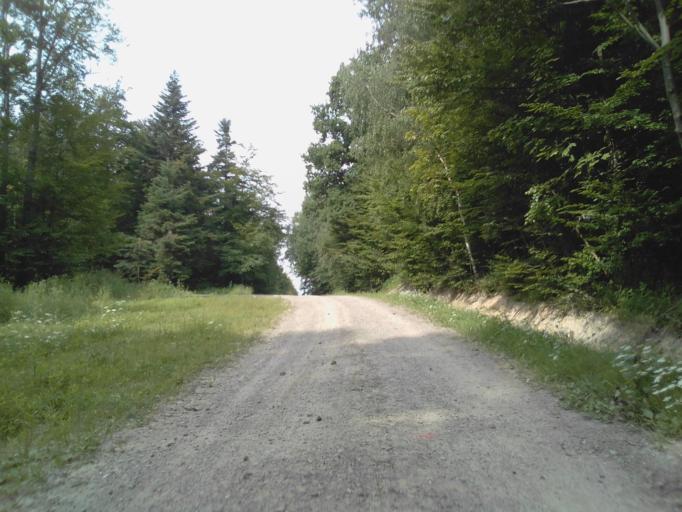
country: PL
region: Subcarpathian Voivodeship
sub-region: Powiat strzyzowski
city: Frysztak
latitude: 49.8793
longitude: 21.5458
